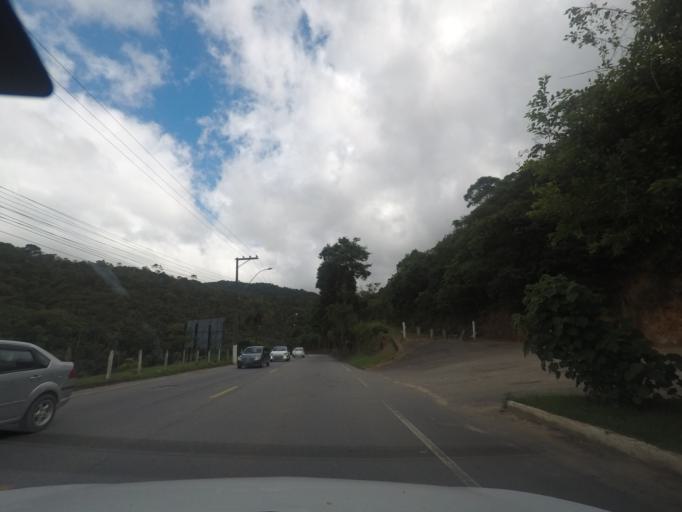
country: BR
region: Rio de Janeiro
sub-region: Teresopolis
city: Teresopolis
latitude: -22.3903
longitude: -42.9572
